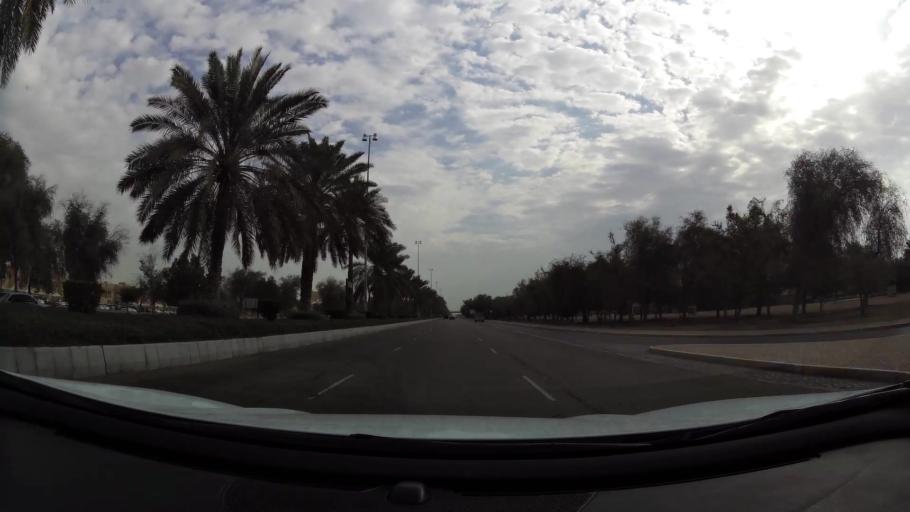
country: AE
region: Abu Dhabi
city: Al Ain
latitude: 24.1985
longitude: 55.6647
